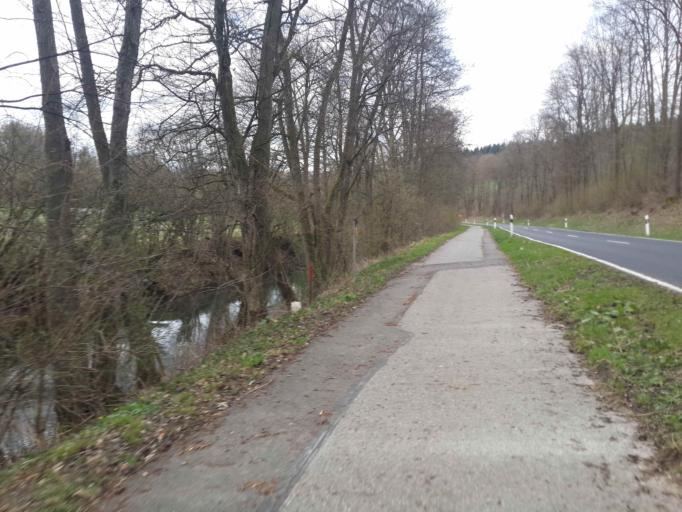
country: DE
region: Baden-Wuerttemberg
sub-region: Karlsruhe Region
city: Adelsheim
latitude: 49.3904
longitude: 9.3937
